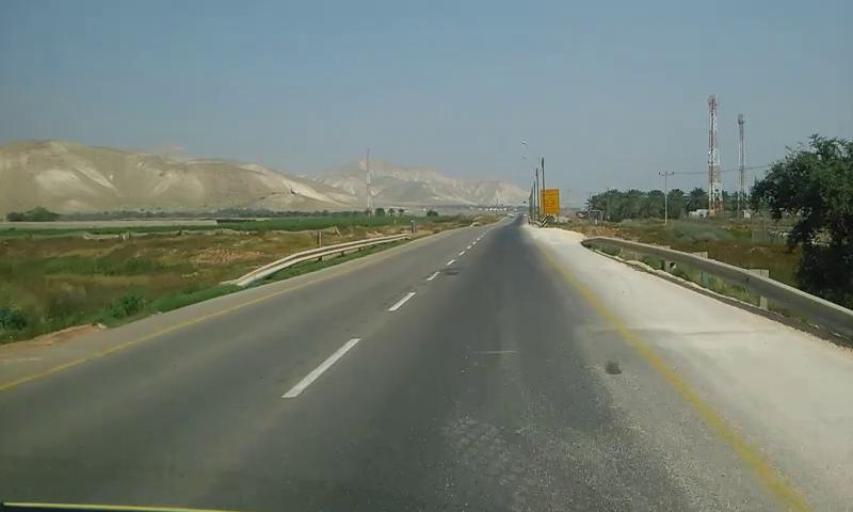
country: PS
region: West Bank
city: Al Fasayil
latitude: 32.0403
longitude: 35.4587
